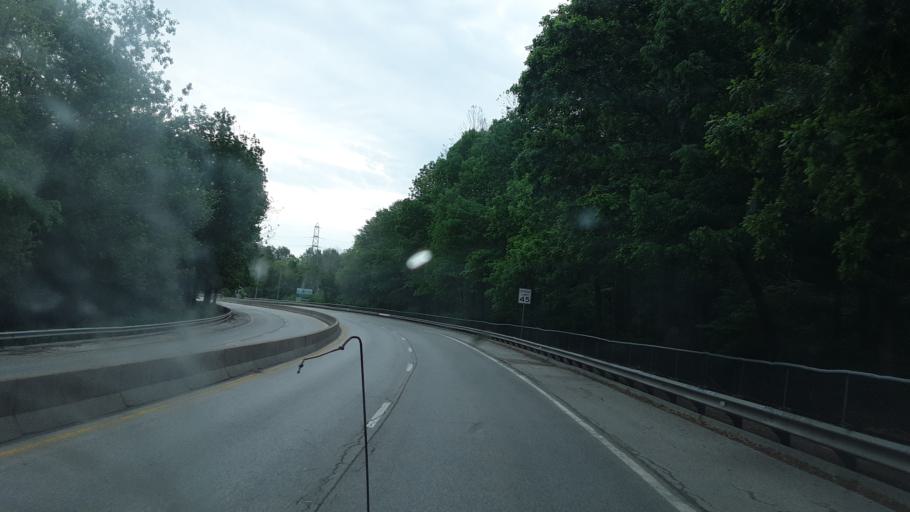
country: US
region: Iowa
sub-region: Lee County
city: Keokuk
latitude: 40.3886
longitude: -91.3672
